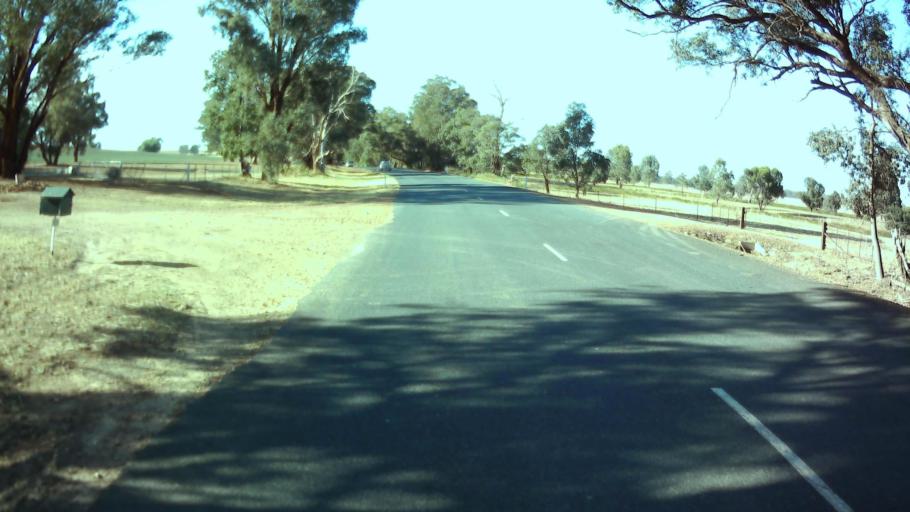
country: AU
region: New South Wales
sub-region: Weddin
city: Grenfell
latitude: -33.9797
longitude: 148.1405
